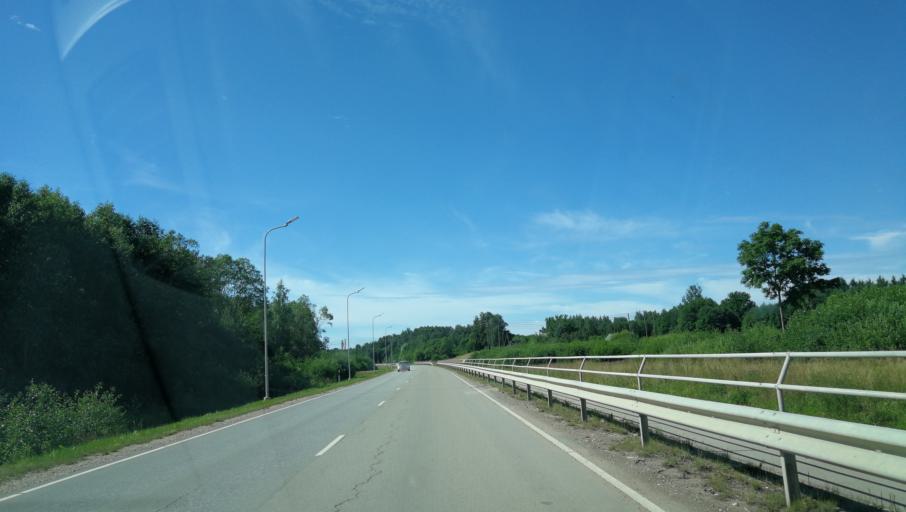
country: LV
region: Gulbenes Rajons
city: Gulbene
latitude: 57.1713
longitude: 26.7397
